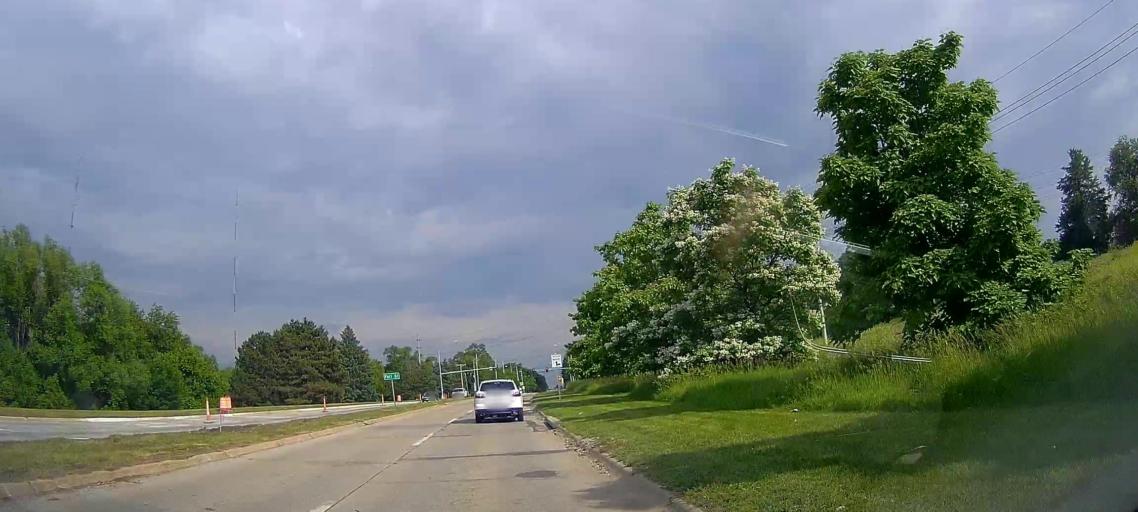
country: US
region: Nebraska
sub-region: Douglas County
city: Ralston
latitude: 41.3077
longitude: -96.0392
